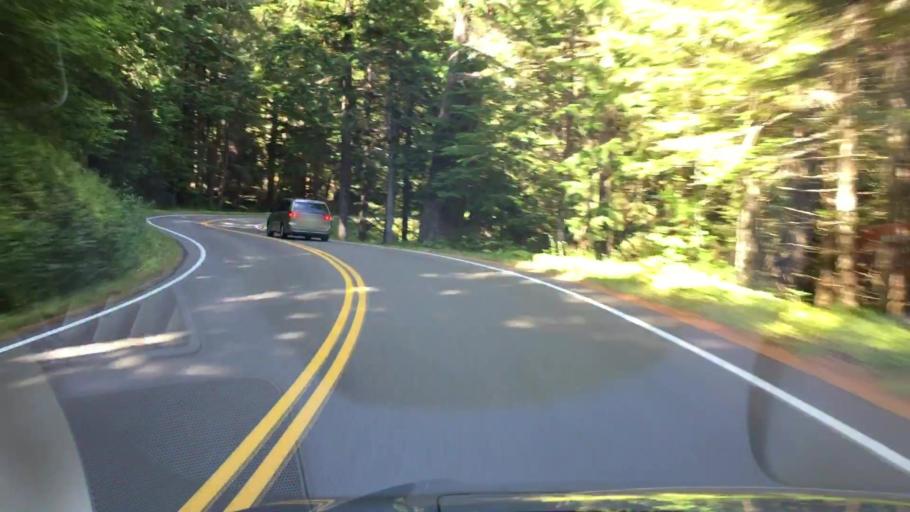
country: US
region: Washington
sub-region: Pierce County
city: Eatonville
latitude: 46.7336
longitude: -121.8314
